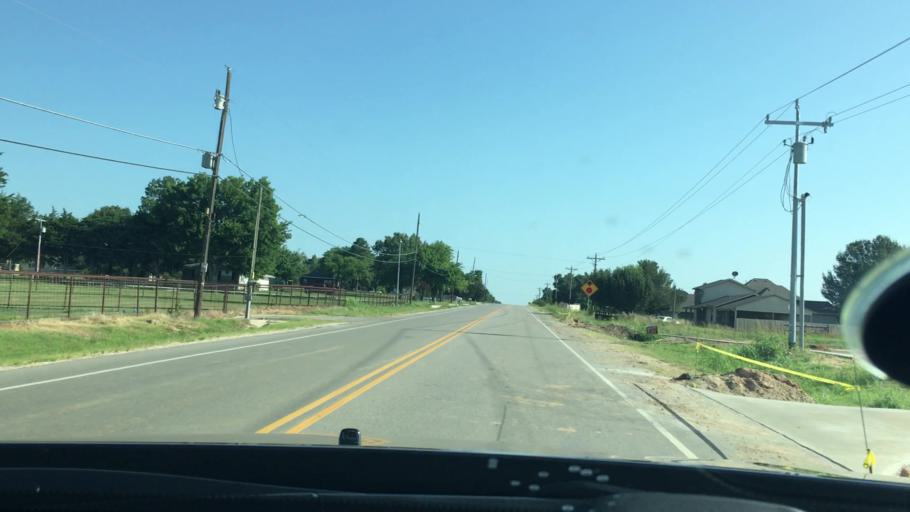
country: US
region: Oklahoma
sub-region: Pontotoc County
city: Ada
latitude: 34.8072
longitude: -96.6523
